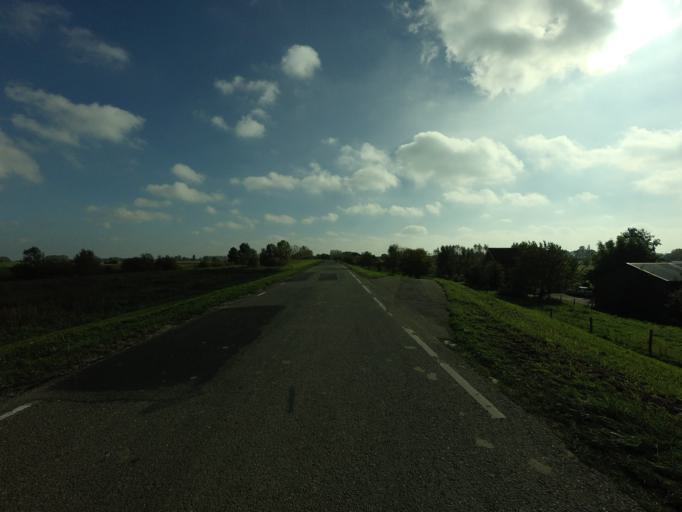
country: NL
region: Gelderland
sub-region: Gemeente Culemborg
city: Culemborg
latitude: 51.9644
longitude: 5.2583
